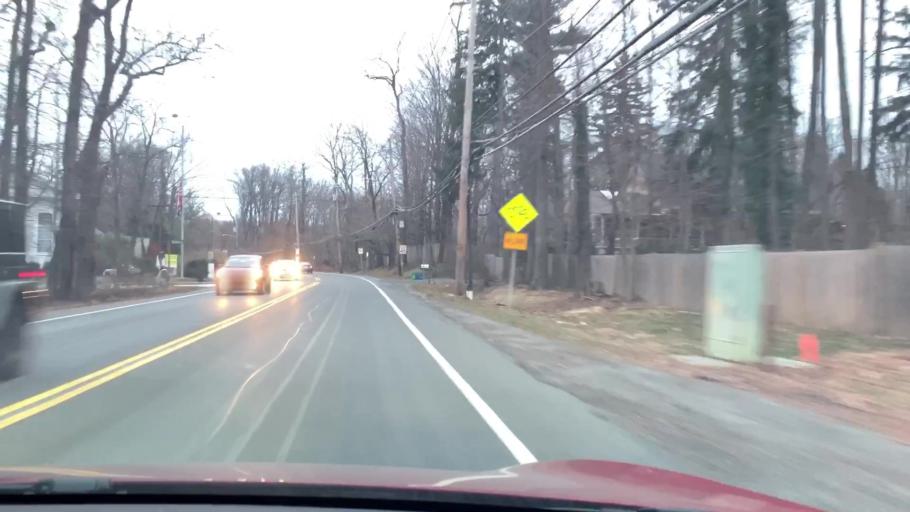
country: US
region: New York
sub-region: Rockland County
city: Sparkill
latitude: 41.0120
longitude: -73.9132
